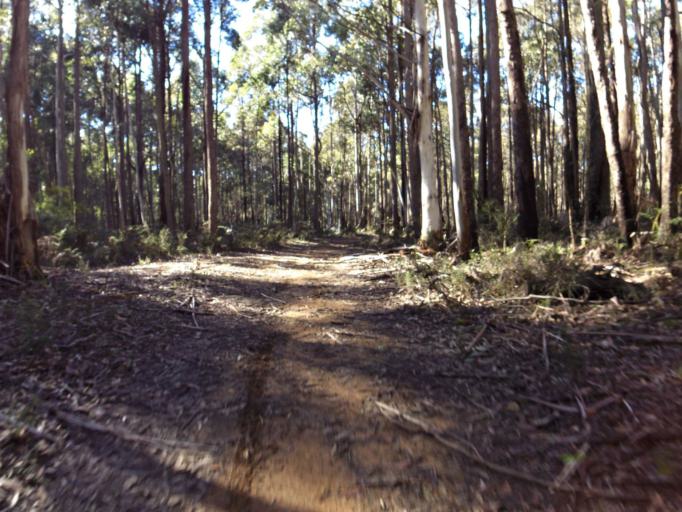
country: AU
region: Victoria
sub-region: Moorabool
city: Bacchus Marsh
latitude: -37.3930
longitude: 144.2811
